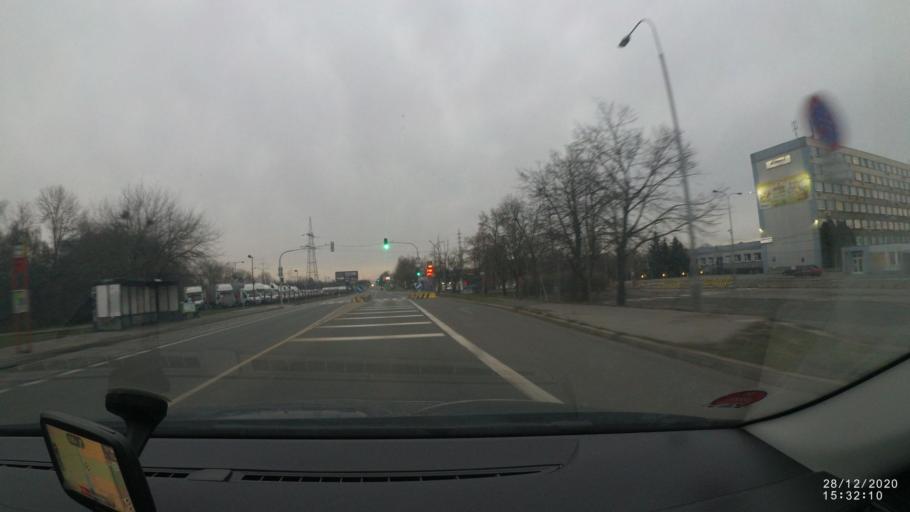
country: CZ
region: Praha
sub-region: Praha 14
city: Hostavice
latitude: 50.0886
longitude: 14.5514
